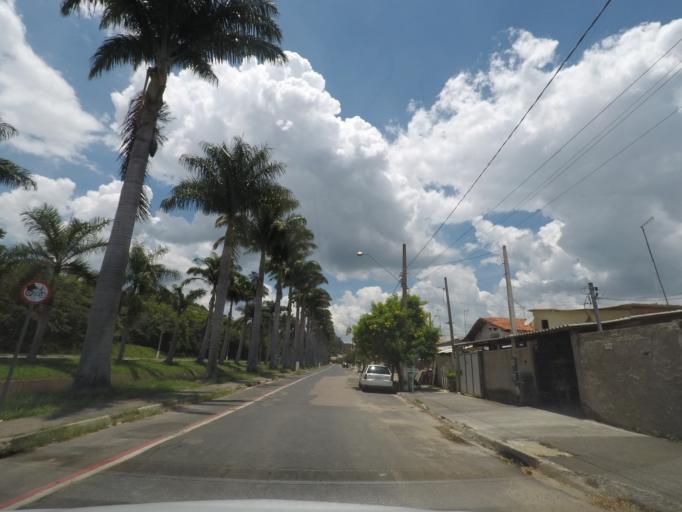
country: BR
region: Sao Paulo
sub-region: Vinhedo
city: Vinhedo
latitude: -23.0249
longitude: -46.9774
